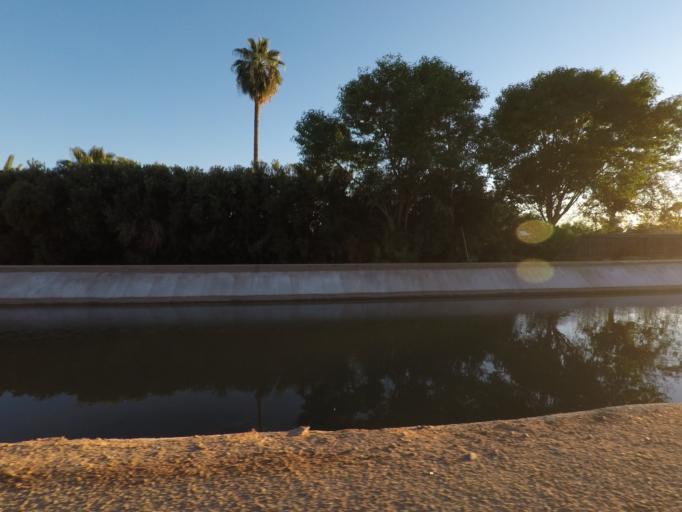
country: US
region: Arizona
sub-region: Maricopa County
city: Phoenix
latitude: 33.5008
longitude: -112.0943
